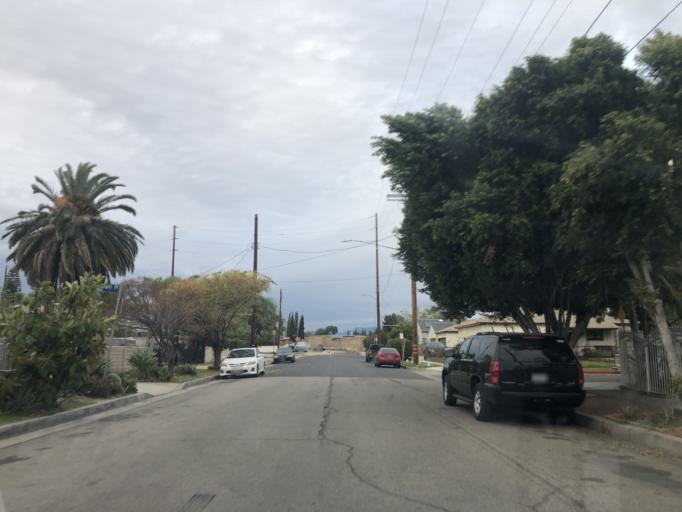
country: US
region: California
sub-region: Los Angeles County
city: North Hollywood
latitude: 34.2195
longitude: -118.3579
